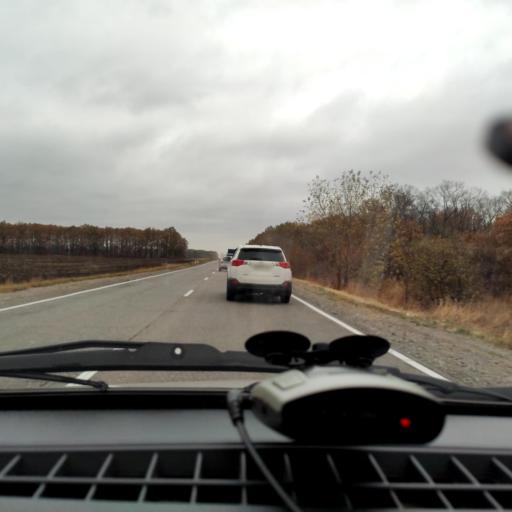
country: RU
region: Voronezj
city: Shilovo
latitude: 51.4174
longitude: 39.0062
